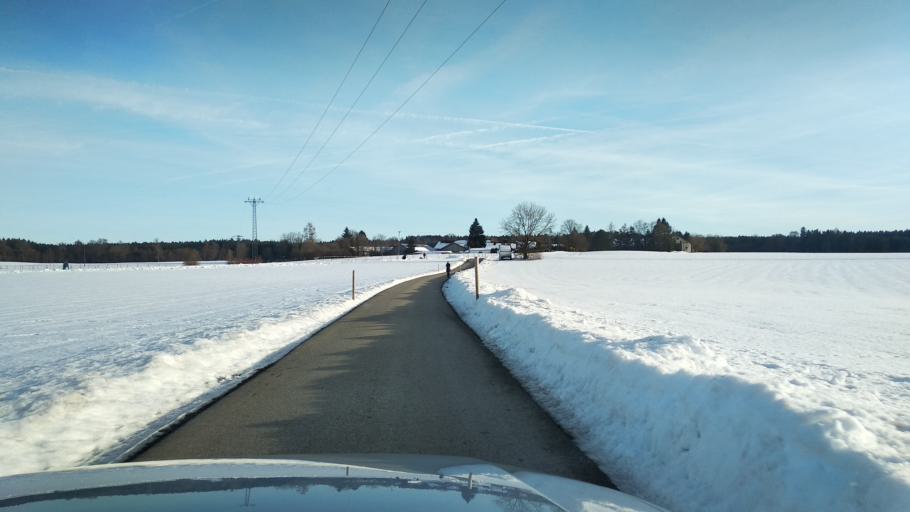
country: DE
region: Bavaria
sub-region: Upper Bavaria
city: Kirchseeon
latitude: 48.0737
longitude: 11.8658
